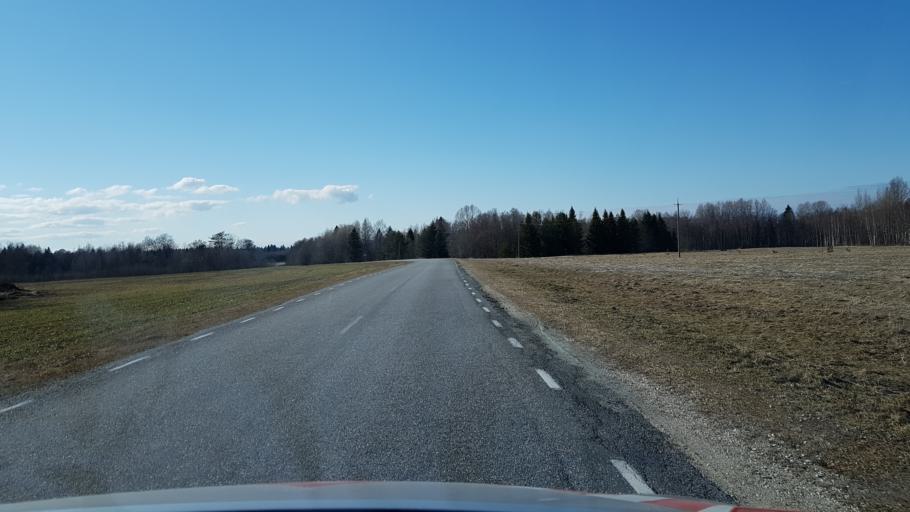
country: EE
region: Laeaene-Virumaa
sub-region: Haljala vald
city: Haljala
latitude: 59.4627
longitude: 26.1953
